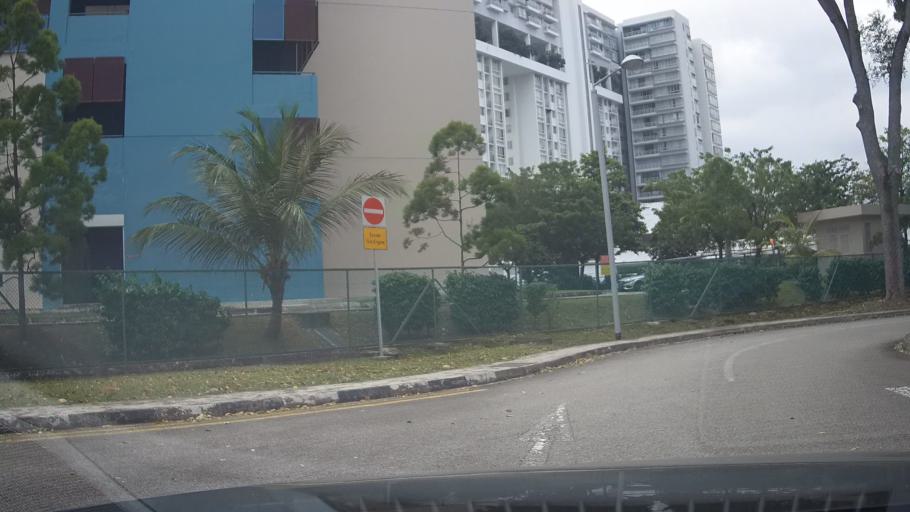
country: SG
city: Singapore
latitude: 1.3014
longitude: 103.8834
